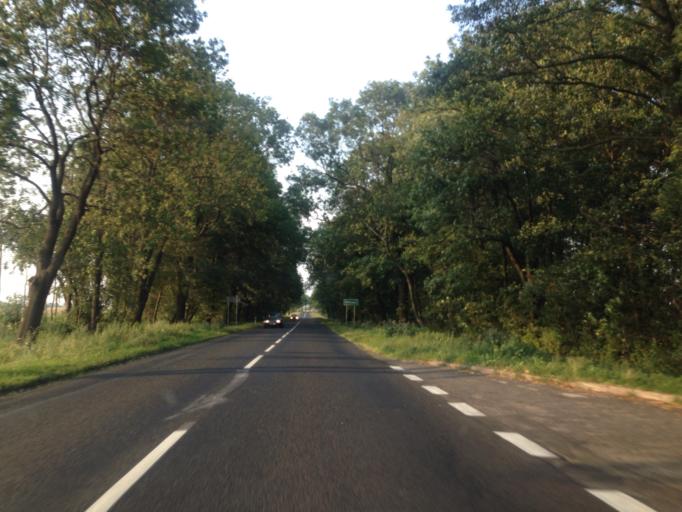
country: PL
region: Kujawsko-Pomorskie
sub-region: Powiat lipnowski
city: Lipno
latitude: 52.8919
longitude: 19.2094
